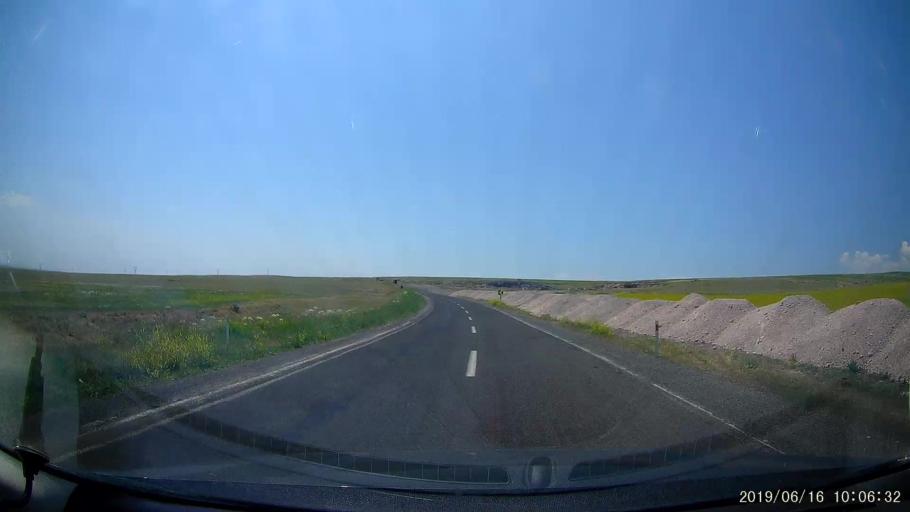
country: TR
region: Kars
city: Digor
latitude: 40.2541
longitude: 43.5432
